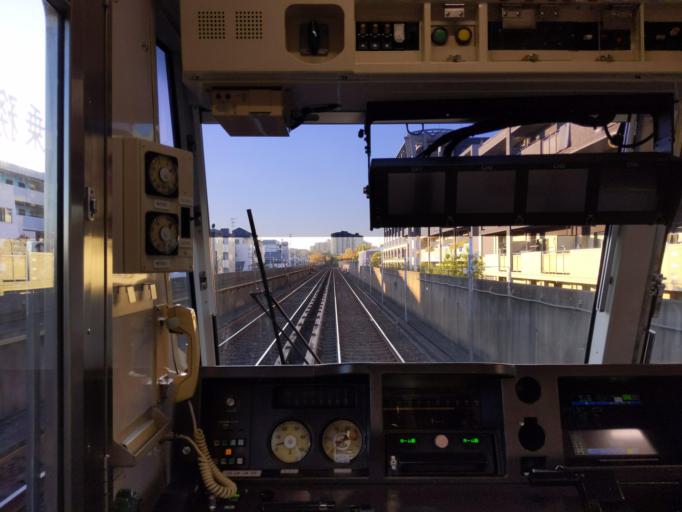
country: JP
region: Kanagawa
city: Yokohama
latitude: 35.5376
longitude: 139.5796
